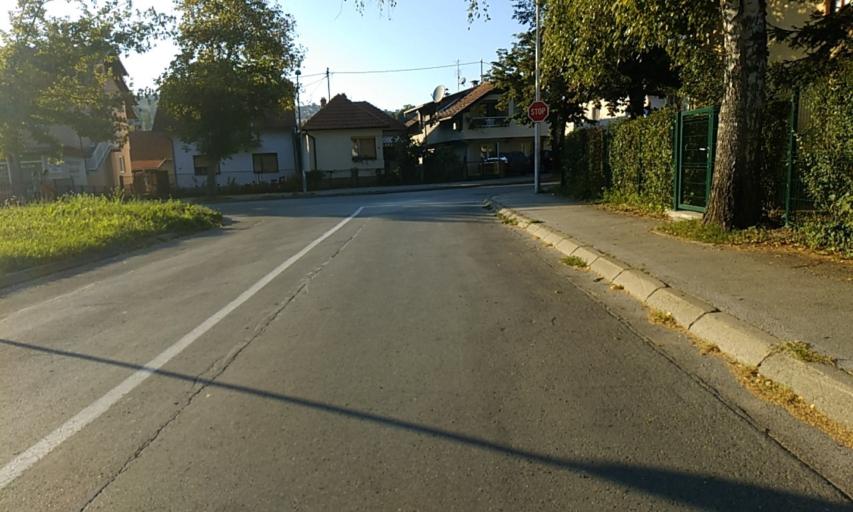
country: BA
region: Republika Srpska
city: Hiseti
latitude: 44.7561
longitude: 17.1819
